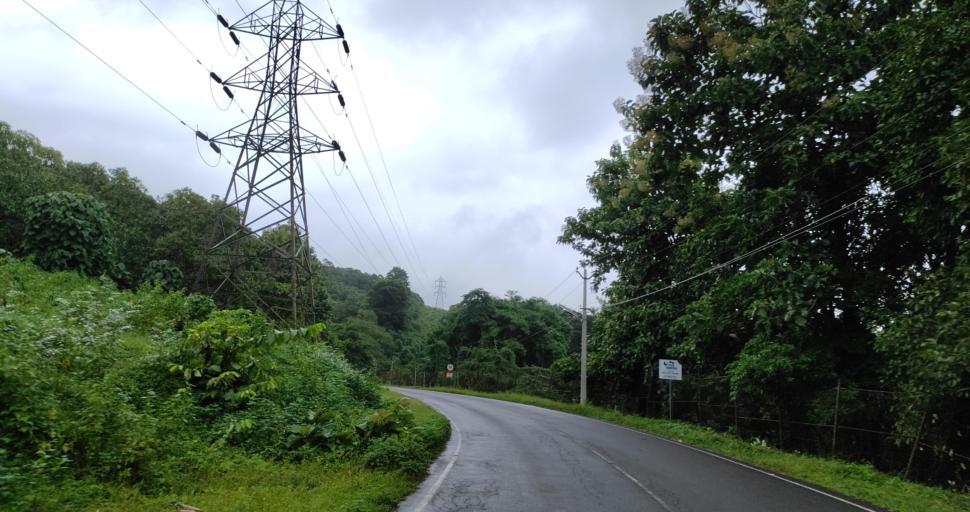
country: IN
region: Kerala
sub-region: Ernakulam
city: Angamali
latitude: 10.2905
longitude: 76.5486
